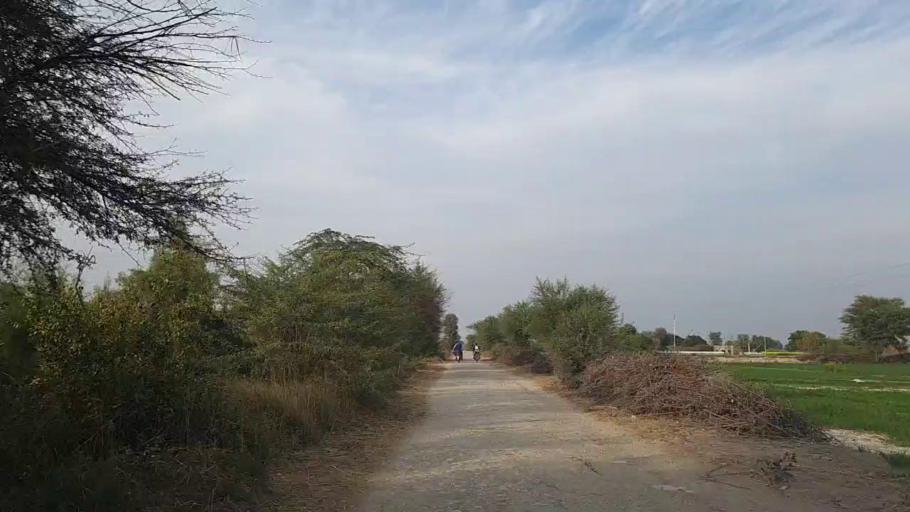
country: PK
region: Sindh
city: Daur
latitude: 26.5212
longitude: 68.4072
